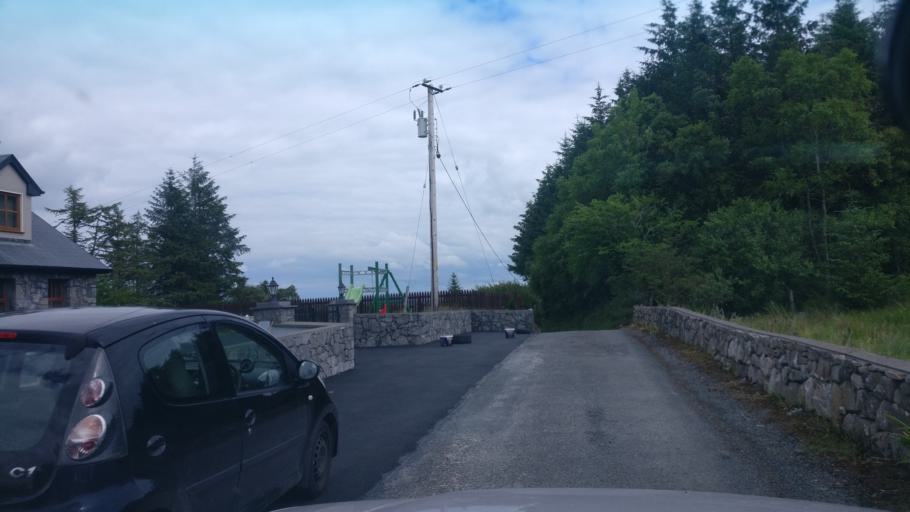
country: IE
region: Connaught
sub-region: County Galway
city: Loughrea
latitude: 53.1425
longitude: -8.5609
